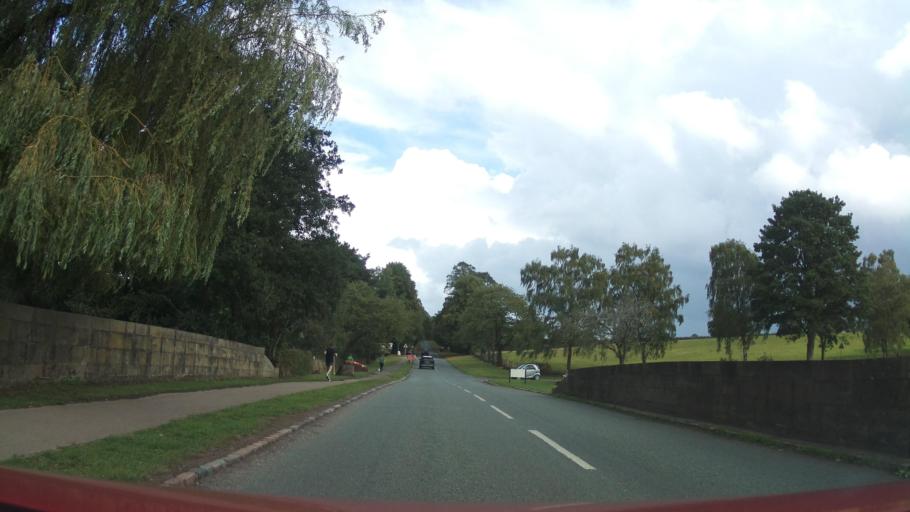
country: GB
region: England
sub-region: Staffordshire
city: Barlaston
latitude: 52.9534
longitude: -2.1634
